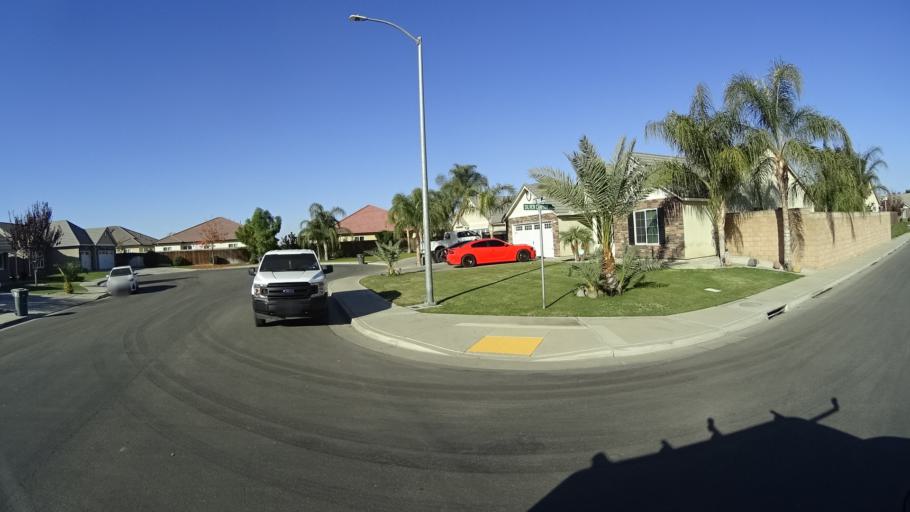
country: US
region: California
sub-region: Kern County
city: Greenfield
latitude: 35.2707
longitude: -119.0440
